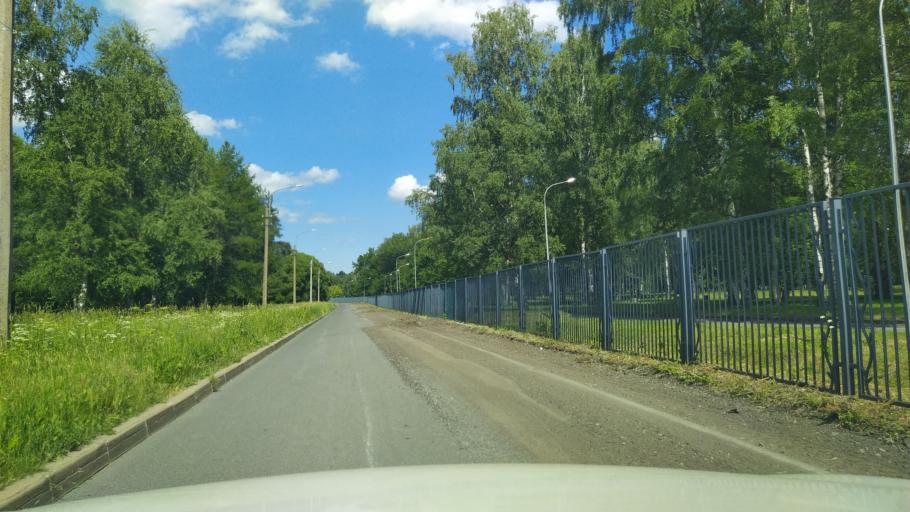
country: RU
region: Leningrad
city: Kalininskiy
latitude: 59.9976
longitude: 30.4164
